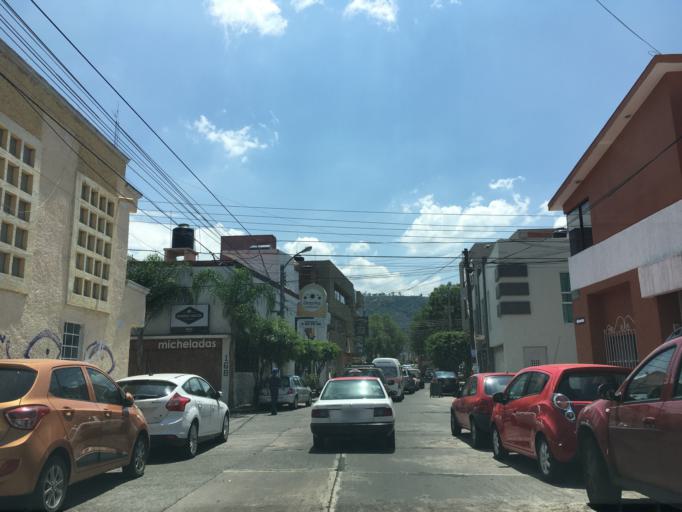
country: MX
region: Michoacan
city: Morelia
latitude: 19.6893
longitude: -101.1641
